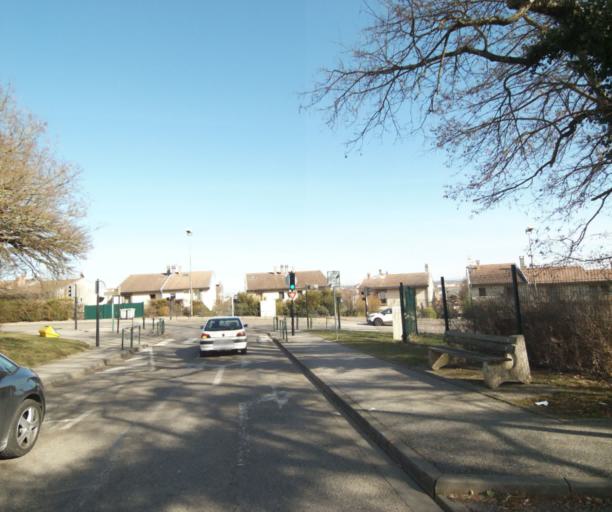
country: FR
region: Lorraine
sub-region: Departement de Meurthe-et-Moselle
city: Villers-les-Nancy
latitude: 48.6707
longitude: 6.1475
